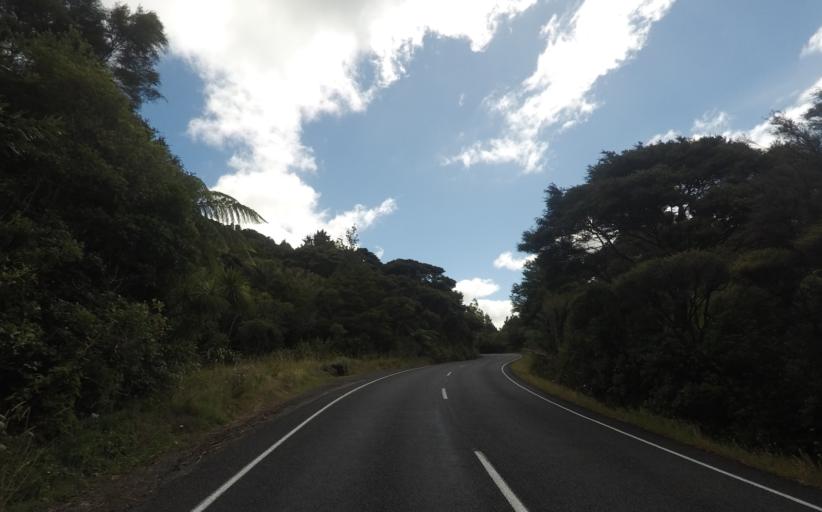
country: NZ
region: Auckland
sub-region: Auckland
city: Muriwai Beach
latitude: -36.8620
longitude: 174.5170
